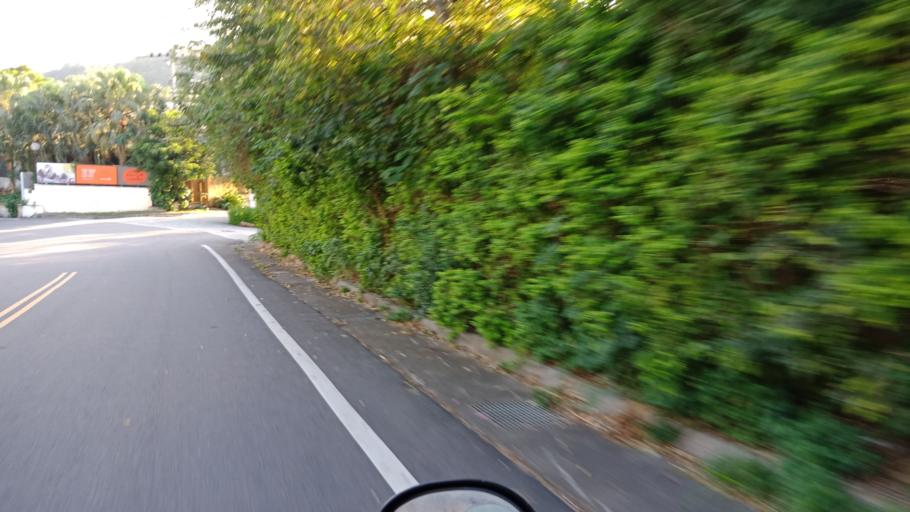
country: TW
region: Taiwan
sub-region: Hsinchu
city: Hsinchu
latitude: 24.7677
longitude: 121.0002
